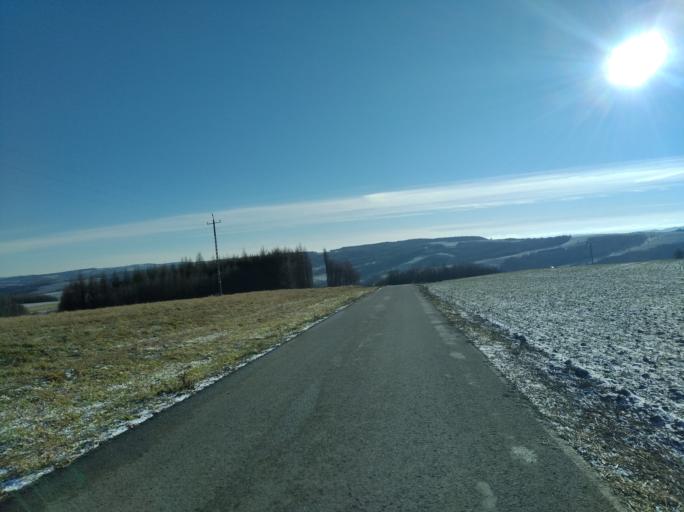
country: PL
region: Subcarpathian Voivodeship
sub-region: Powiat strzyzowski
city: Czudec
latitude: 49.9410
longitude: 21.7674
